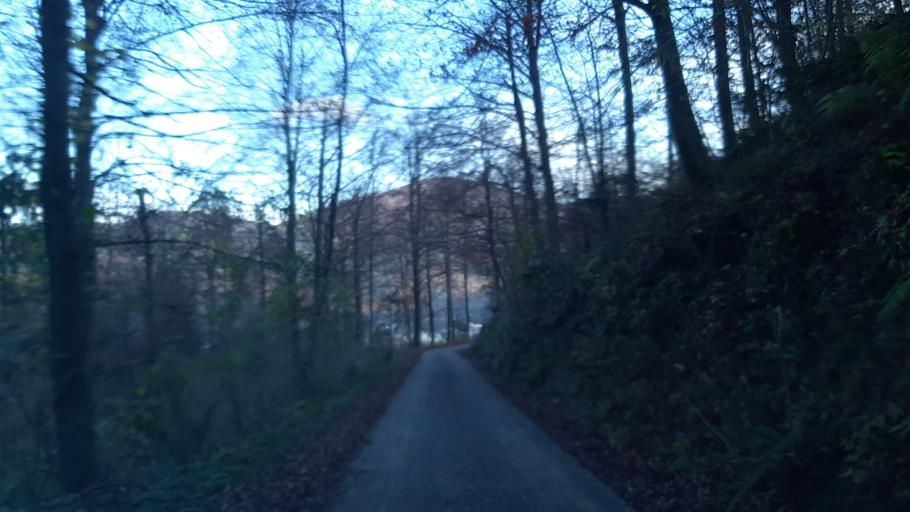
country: SI
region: Borovnica
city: Borovnica
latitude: 45.9230
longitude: 14.3493
